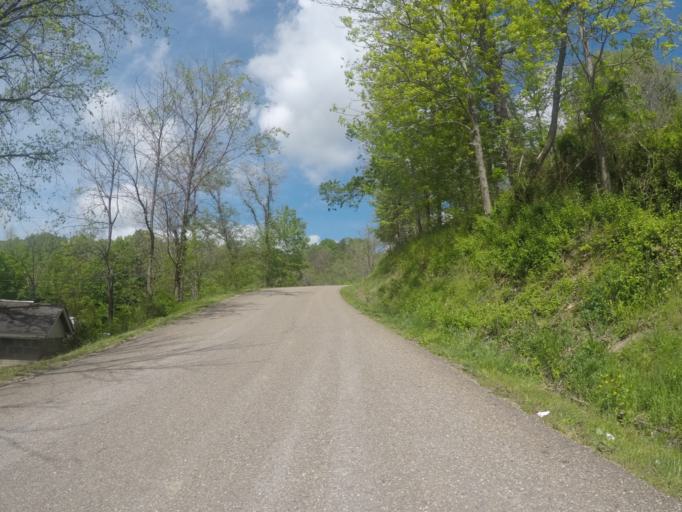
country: US
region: West Virginia
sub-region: Cabell County
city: Huntington
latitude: 38.5324
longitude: -82.4399
